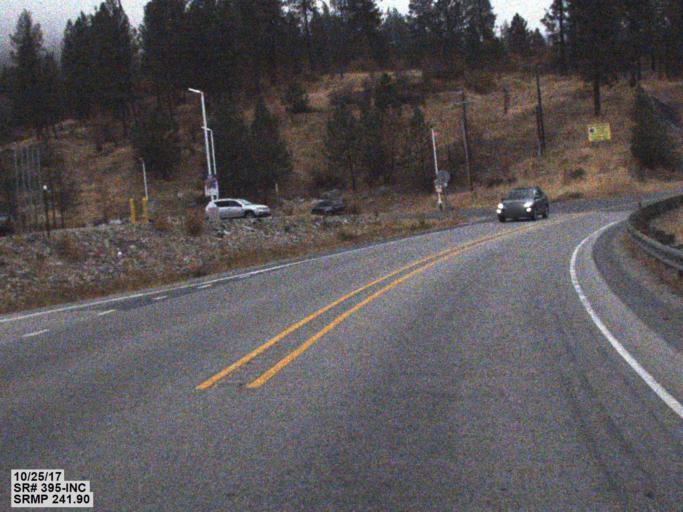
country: US
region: Washington
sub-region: Stevens County
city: Kettle Falls
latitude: 48.6275
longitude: -118.1228
